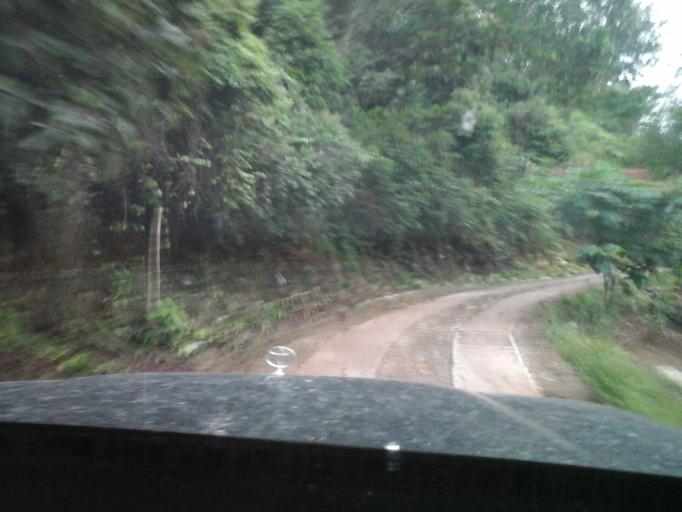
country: CO
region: Cesar
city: Agustin Codazzi
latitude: 9.9398
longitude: -73.1316
